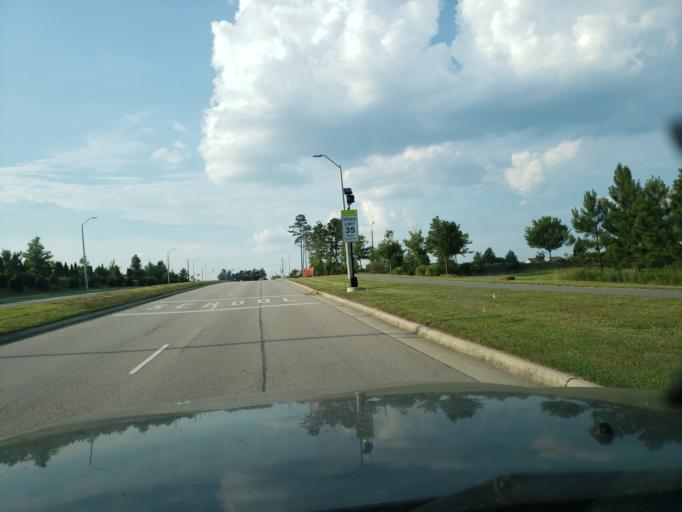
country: US
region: North Carolina
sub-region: Wake County
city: Green Level
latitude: 35.8407
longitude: -78.9102
